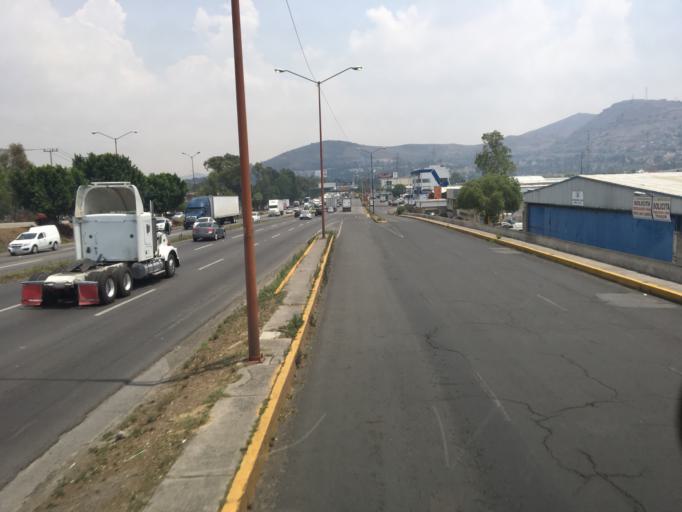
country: MX
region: Mexico
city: Tlalnepantla
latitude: 19.5472
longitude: -99.1832
